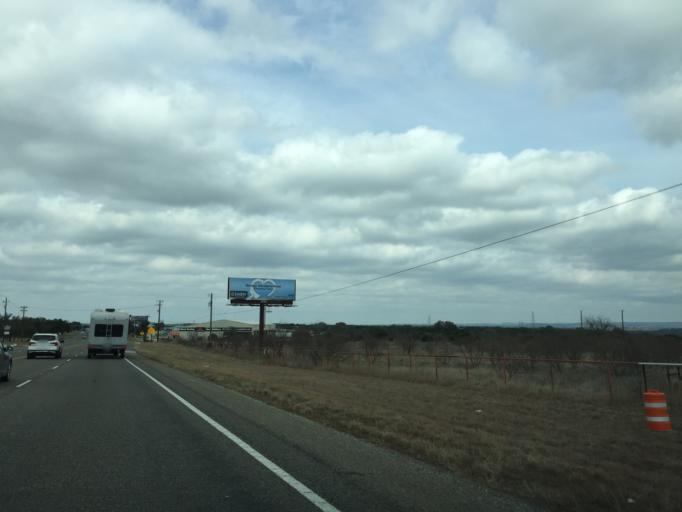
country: US
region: Texas
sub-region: Travis County
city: Briarcliff
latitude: 30.4570
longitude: -98.1537
